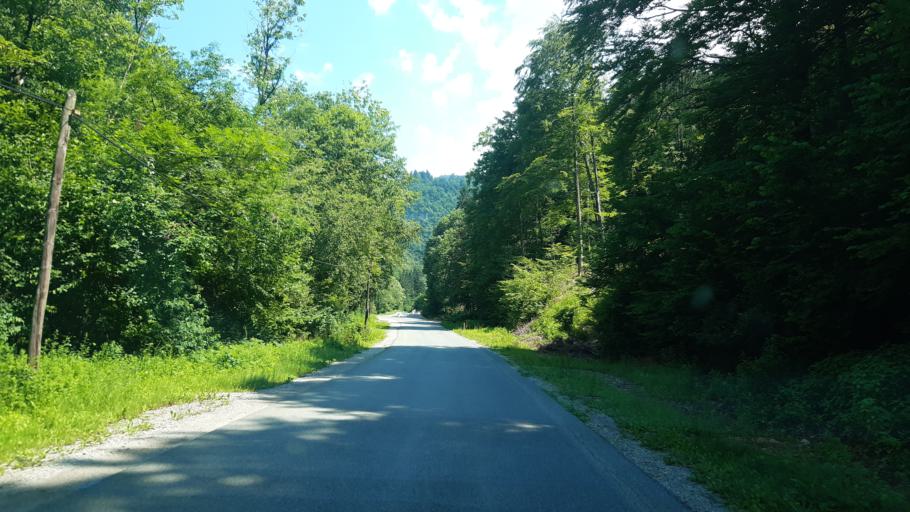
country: SI
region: Cerklje na Gorenjskem
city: Cerklje na Gorenjskem
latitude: 46.2719
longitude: 14.4932
